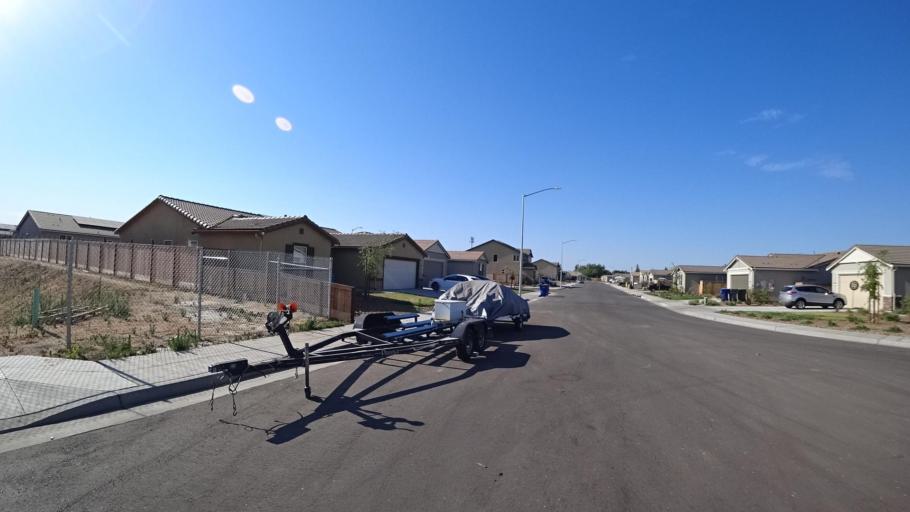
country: US
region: California
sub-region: Fresno County
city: Sunnyside
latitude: 36.7672
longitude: -119.6635
